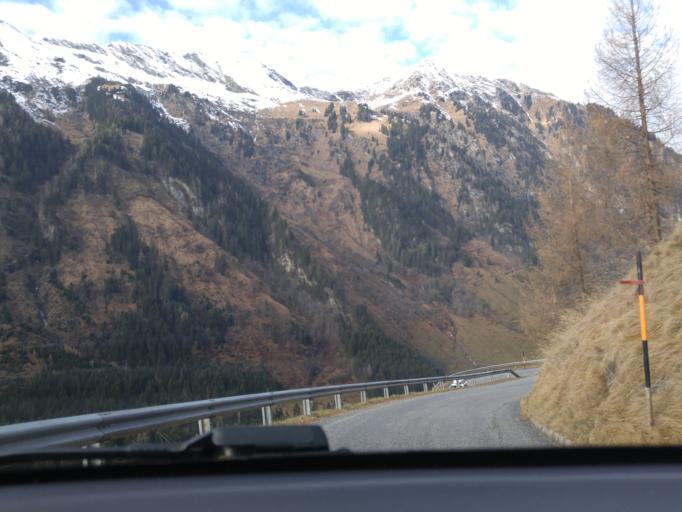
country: AT
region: Salzburg
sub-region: Politischer Bezirk Zell am See
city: Uttendorf
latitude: 47.2004
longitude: 12.6078
